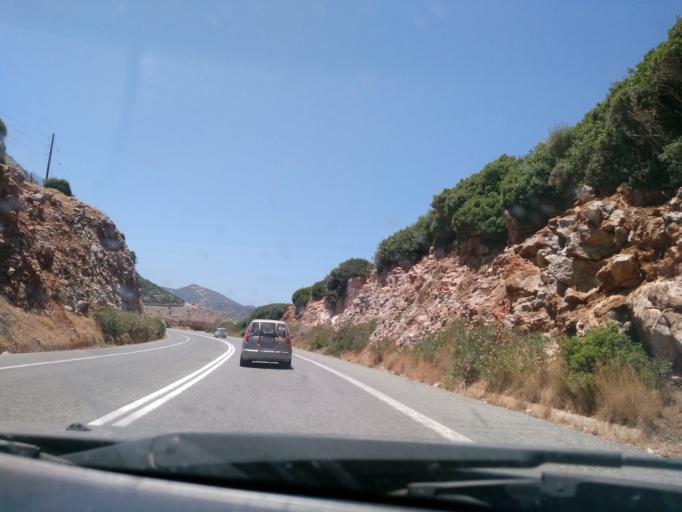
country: GR
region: Crete
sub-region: Nomos Rethymnis
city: Zoniana
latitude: 35.4087
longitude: 24.8247
